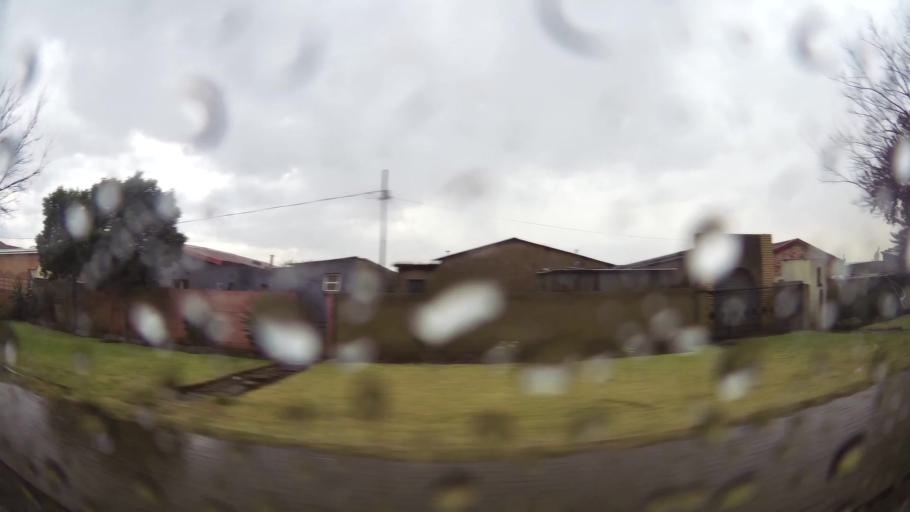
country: ZA
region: Gauteng
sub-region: Ekurhuleni Metropolitan Municipality
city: Germiston
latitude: -26.3593
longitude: 28.1382
